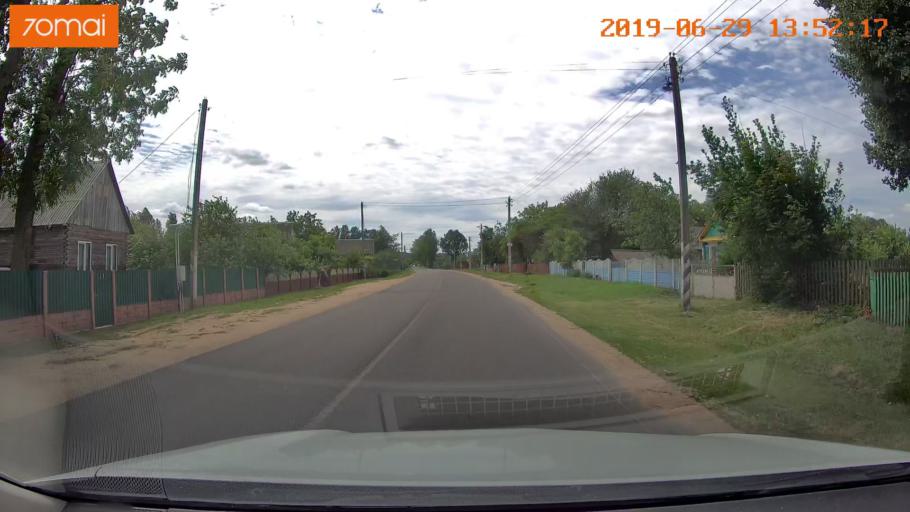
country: BY
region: Minsk
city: Slutsk
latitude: 52.9964
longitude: 27.5566
